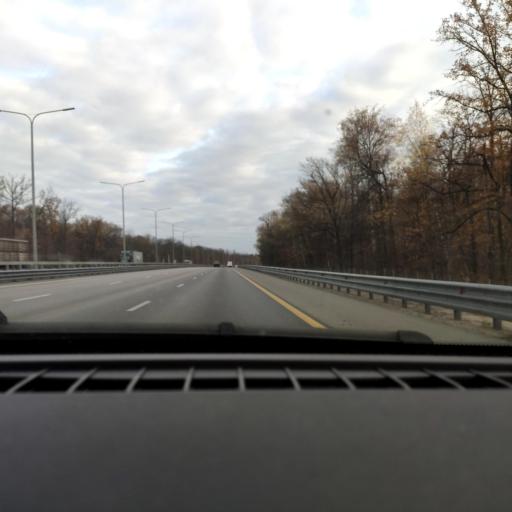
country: RU
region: Voronezj
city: Podgornoye
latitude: 51.8328
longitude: 39.2356
